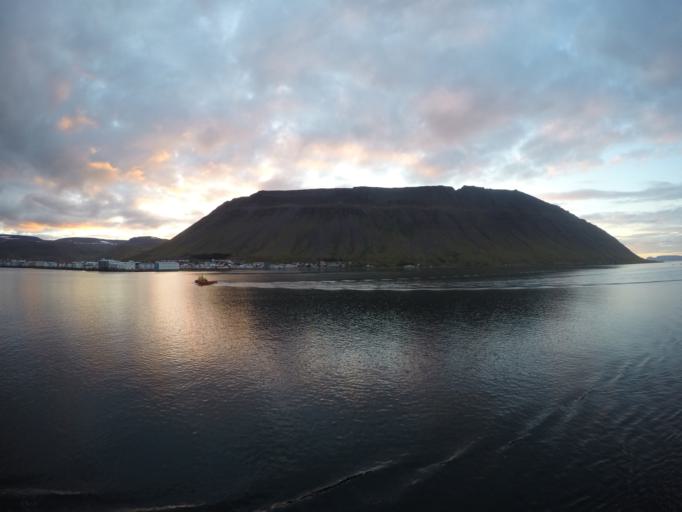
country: IS
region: Westfjords
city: Isafjoerdur
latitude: 66.0730
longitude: -23.1026
